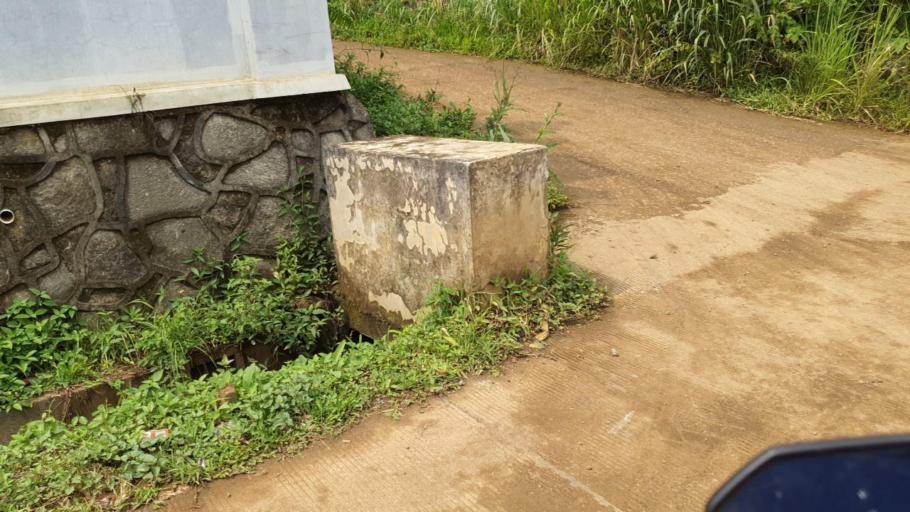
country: ID
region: West Java
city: Caringin
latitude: -6.6557
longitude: 106.8840
